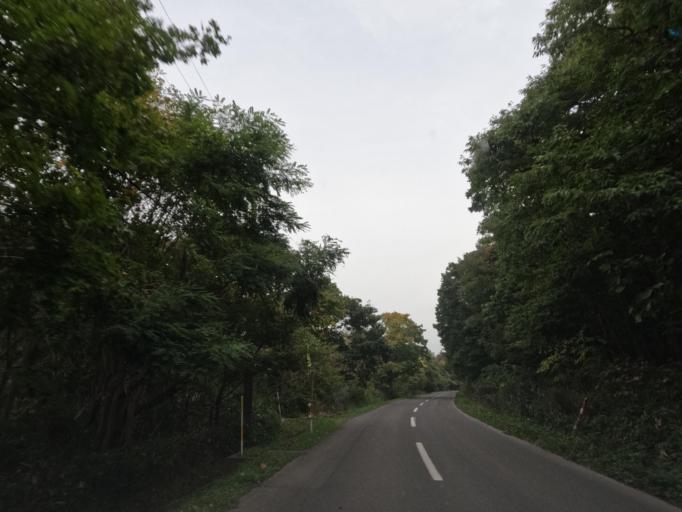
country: JP
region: Hokkaido
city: Date
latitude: 42.3997
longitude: 140.9302
